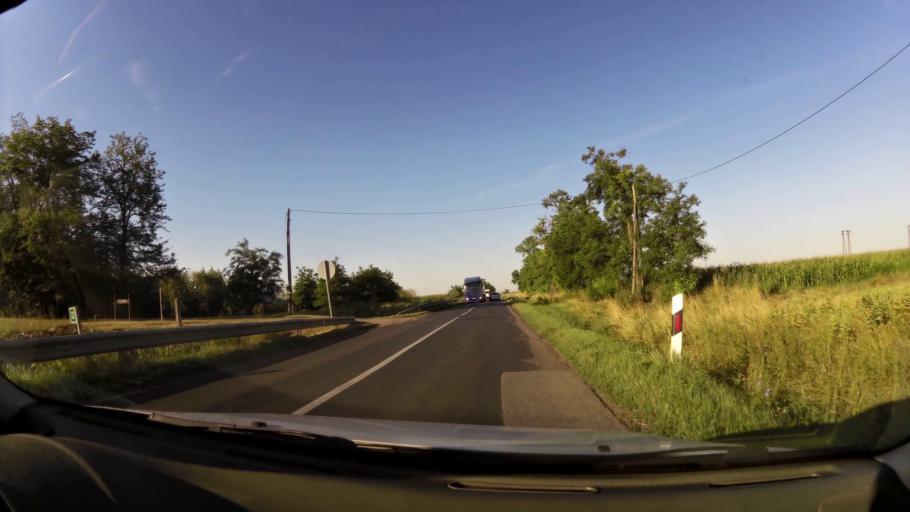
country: HU
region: Pest
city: Tapioszolos
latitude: 47.2730
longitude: 19.8647
